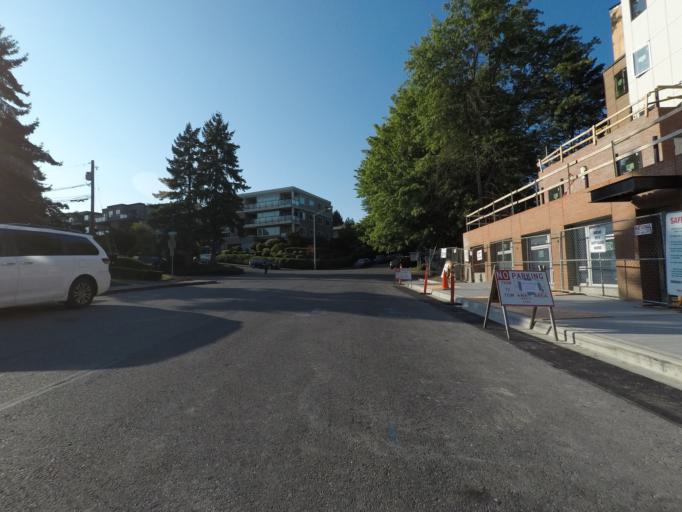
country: US
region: Washington
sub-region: King County
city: Kirkland
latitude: 47.6786
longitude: -122.2013
